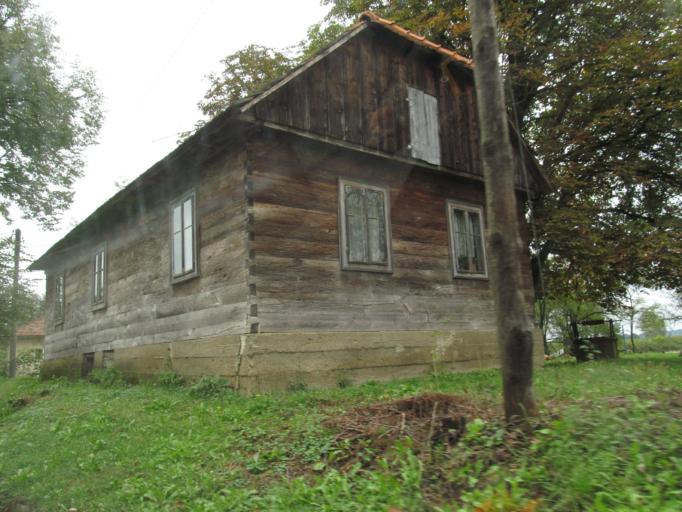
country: HR
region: Grad Zagreb
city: Horvati
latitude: 45.5348
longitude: 15.7913
